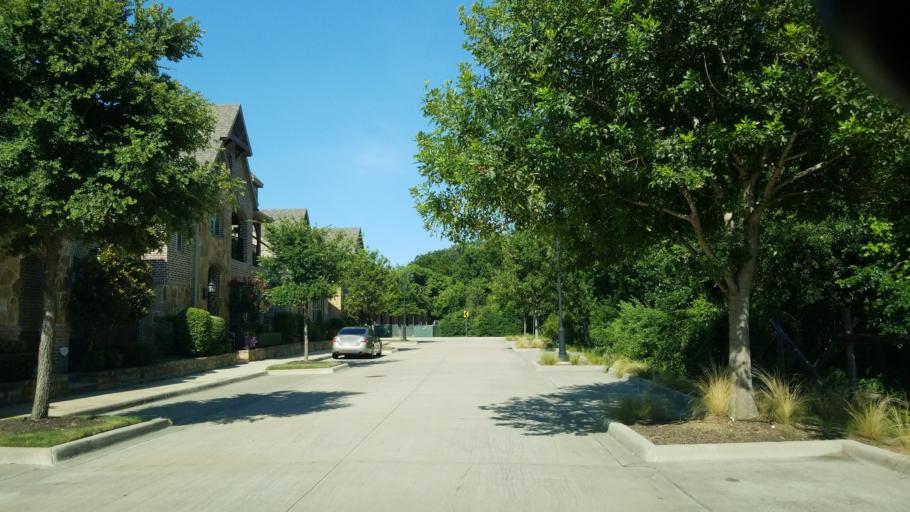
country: US
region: Texas
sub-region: Dallas County
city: Farmers Branch
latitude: 32.9203
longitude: -96.8947
